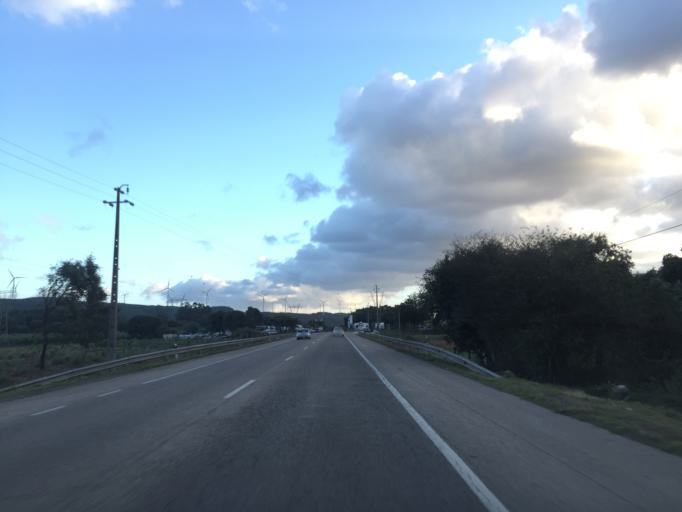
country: PT
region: Leiria
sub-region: Alcobaca
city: Benedita
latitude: 39.4127
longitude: -8.9627
